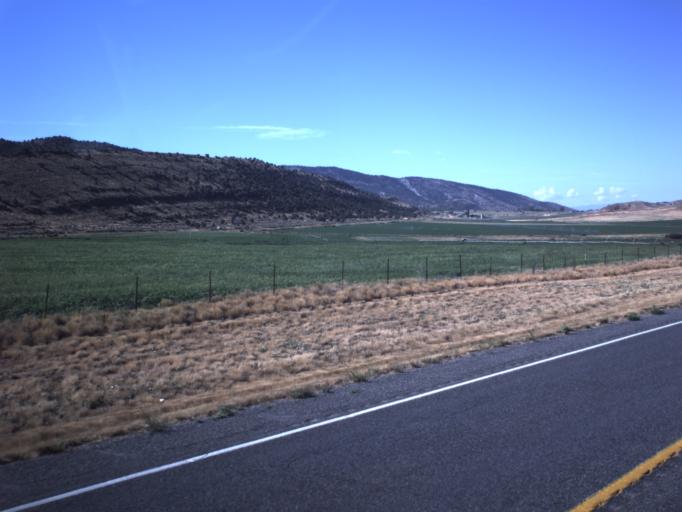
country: US
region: Utah
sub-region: Sanpete County
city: Manti
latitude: 39.2277
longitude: -111.6712
